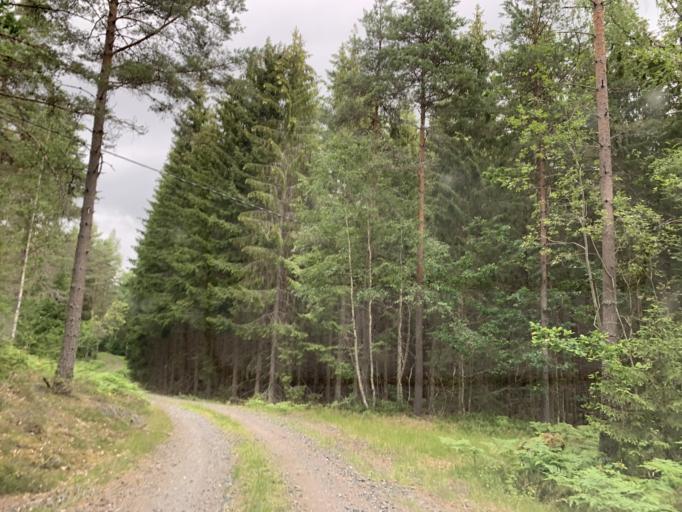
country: SE
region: Kalmar
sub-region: Vasterviks Kommun
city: Overum
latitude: 58.0248
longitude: 16.1162
